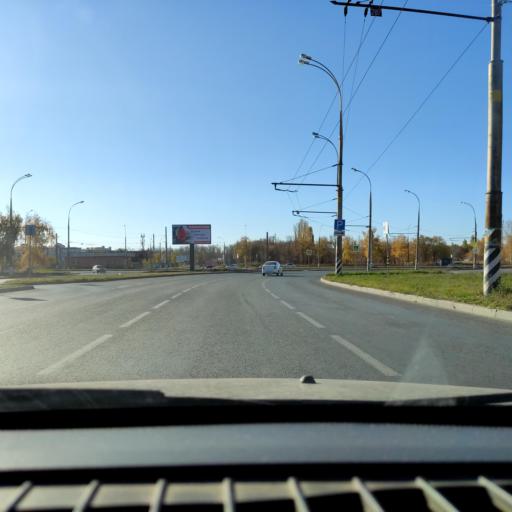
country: RU
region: Samara
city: Tol'yatti
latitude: 53.4996
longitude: 49.2899
